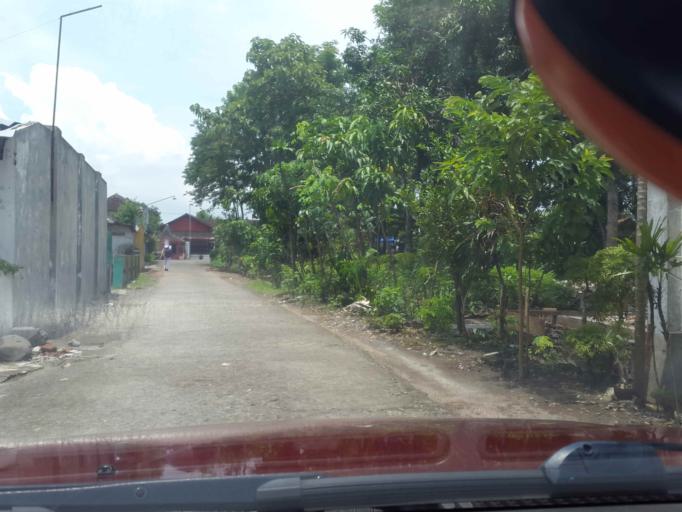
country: ID
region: Central Java
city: Jaten
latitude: -7.6064
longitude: 110.9771
